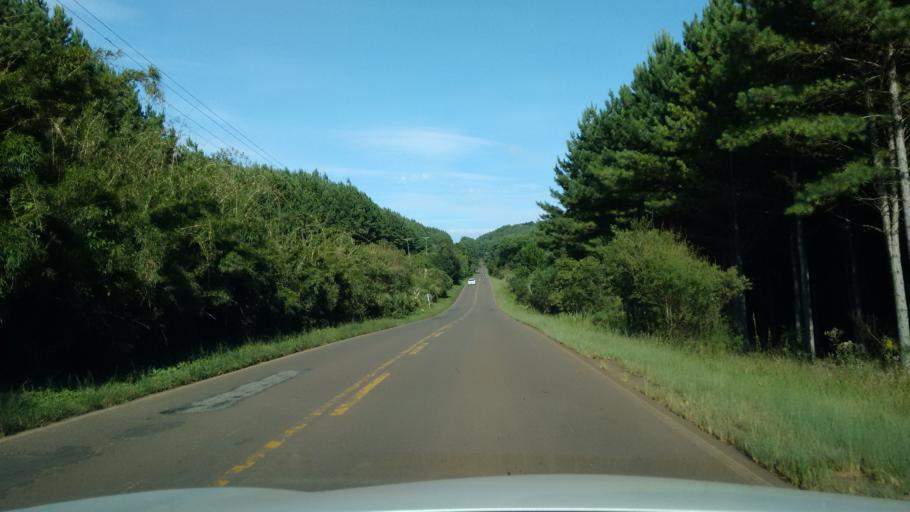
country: BR
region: Santa Catarina
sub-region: Videira
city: Videira
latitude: -27.1141
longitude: -50.9232
